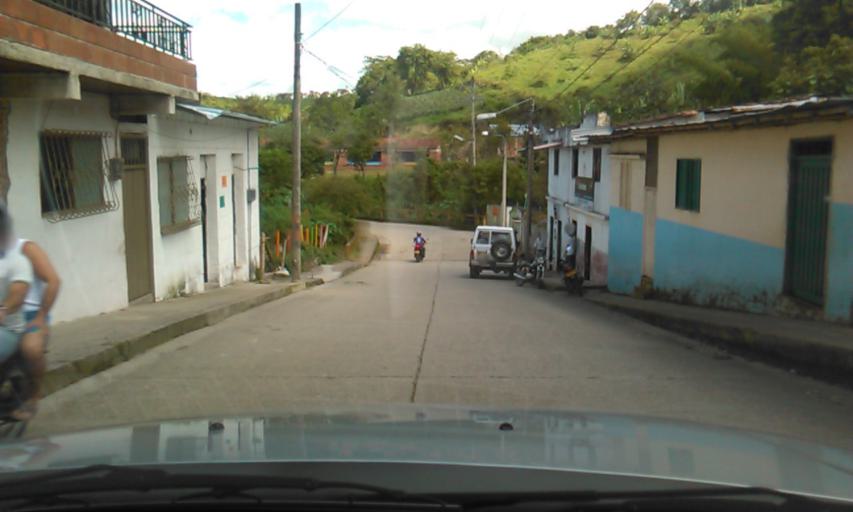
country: CO
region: Quindio
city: Cordoba
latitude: 4.3918
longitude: -75.6871
